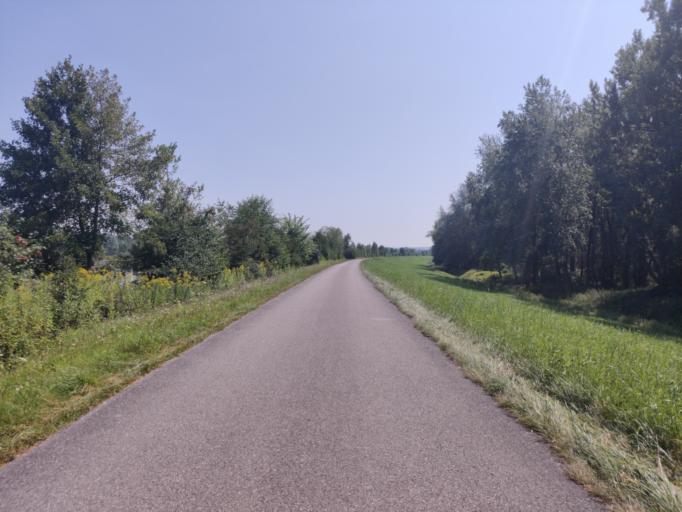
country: AT
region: Upper Austria
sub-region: Politischer Bezirk Urfahr-Umgebung
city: Goldworth
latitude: 48.3135
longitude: 14.0955
